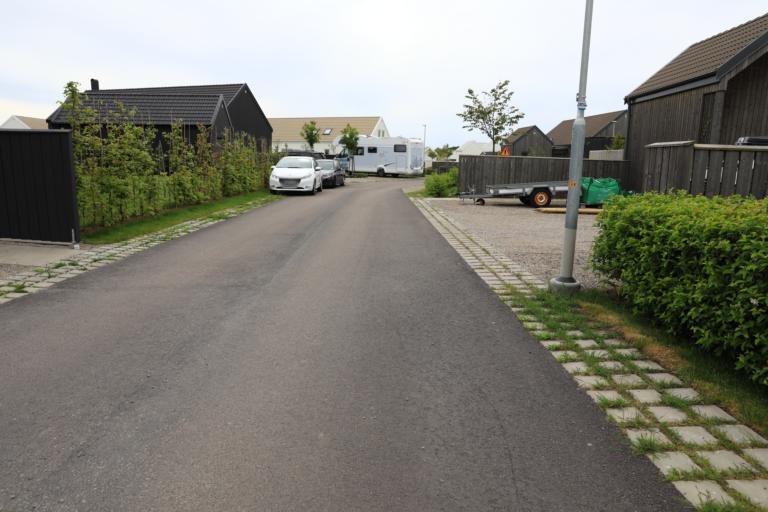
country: SE
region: Halland
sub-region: Varbergs Kommun
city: Varberg
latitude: 57.1478
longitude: 12.2395
